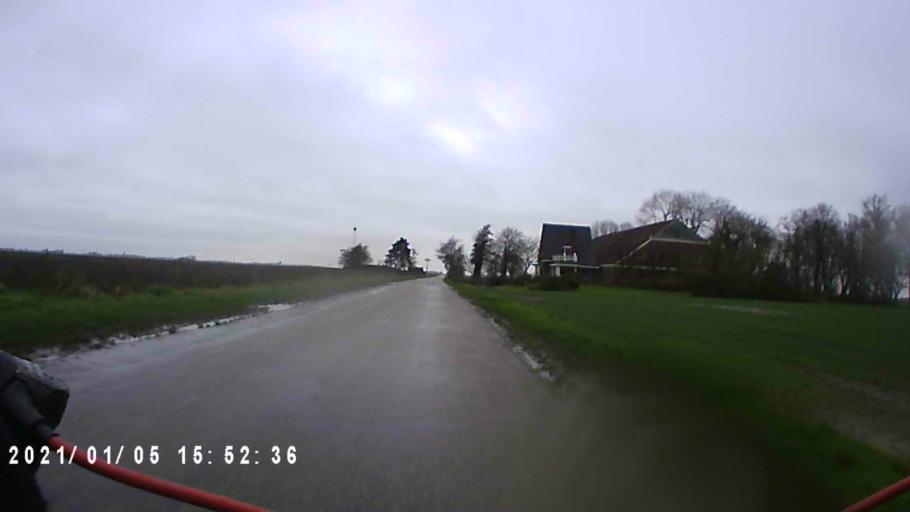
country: NL
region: Groningen
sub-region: Gemeente  Oldambt
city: Winschoten
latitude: 53.2030
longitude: 7.1003
